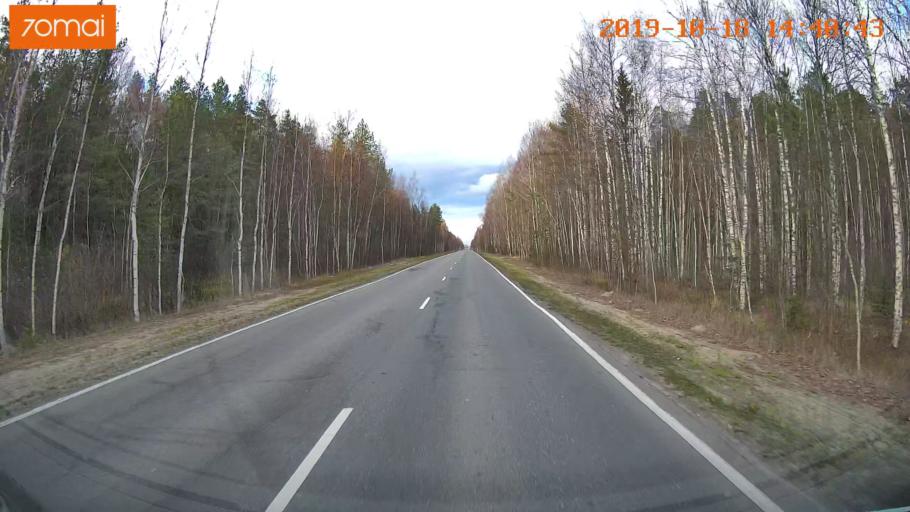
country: RU
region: Vladimir
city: Velikodvorskiy
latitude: 55.2808
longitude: 40.6695
